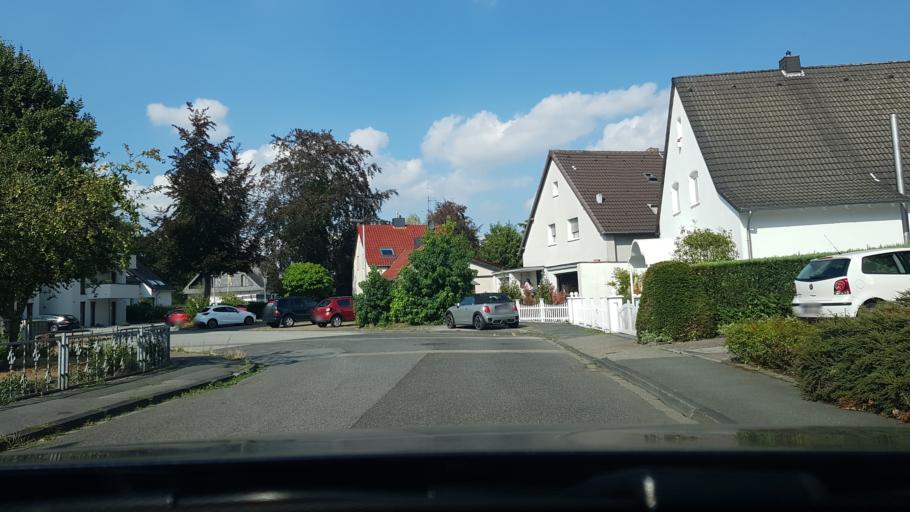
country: DE
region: North Rhine-Westphalia
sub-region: Regierungsbezirk Dusseldorf
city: Muelheim (Ruhr)
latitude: 51.4105
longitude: 6.8586
